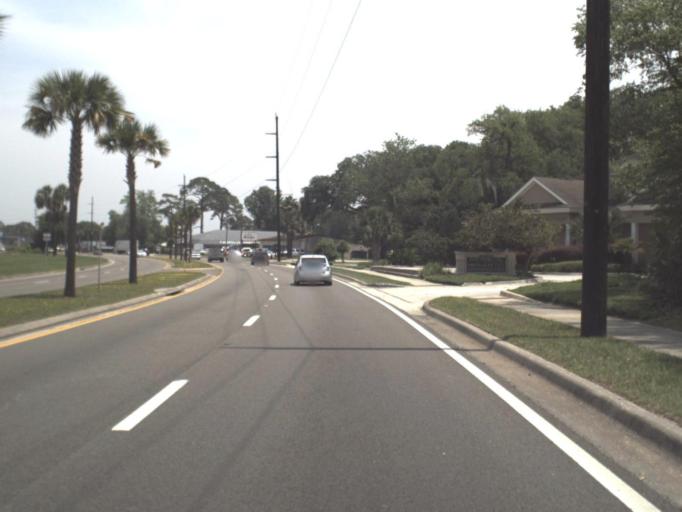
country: US
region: Florida
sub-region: Nassau County
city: Fernandina Beach
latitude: 30.6349
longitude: -81.4596
